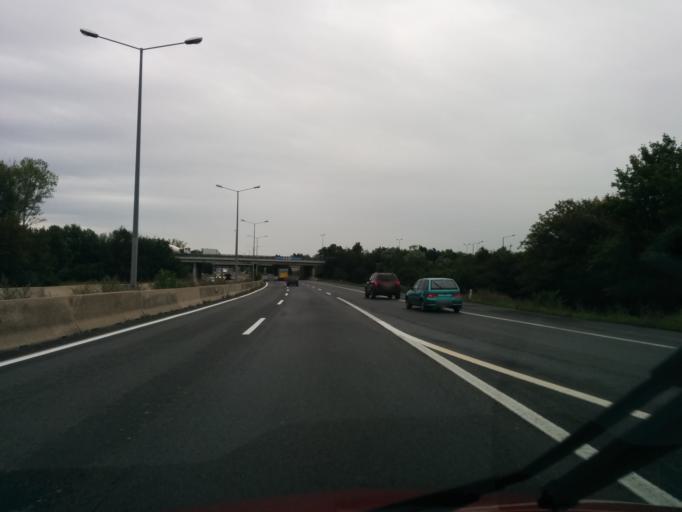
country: AT
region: Lower Austria
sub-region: Politischer Bezirk Modling
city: Brunn am Gebirge
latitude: 48.1166
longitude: 16.2953
